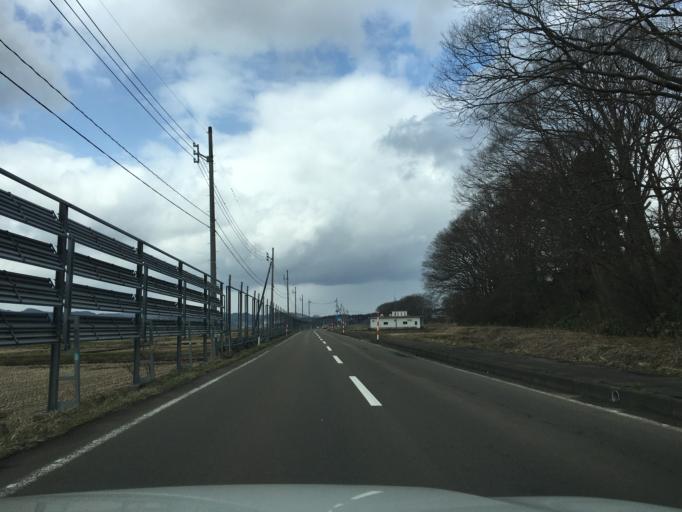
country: JP
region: Akita
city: Takanosu
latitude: 40.1468
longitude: 140.3431
